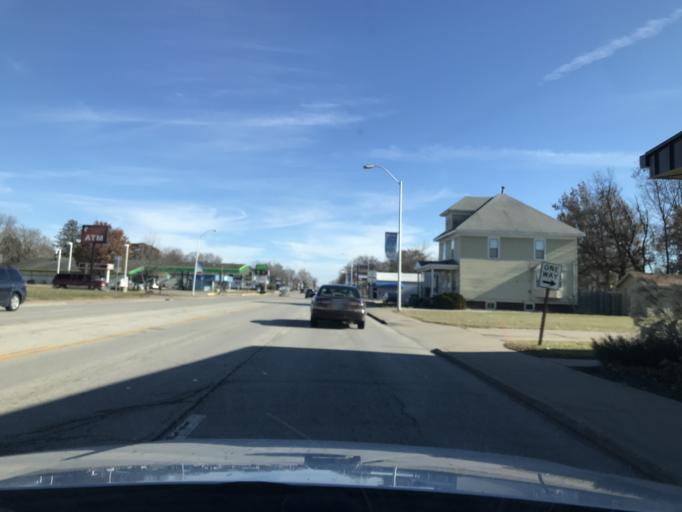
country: US
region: Illinois
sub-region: McDonough County
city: Macomb
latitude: 40.4587
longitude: -90.6657
